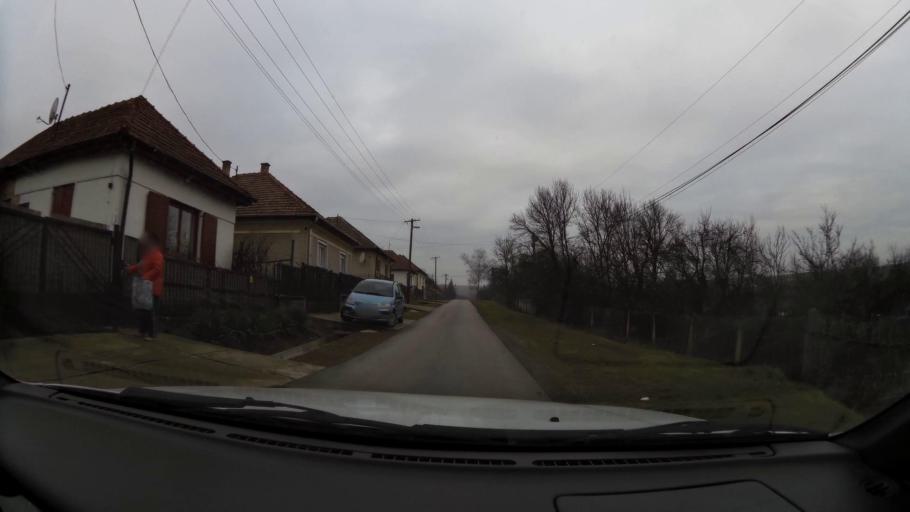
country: HU
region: Borsod-Abauj-Zemplen
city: Rudabanya
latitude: 48.4121
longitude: 20.6523
